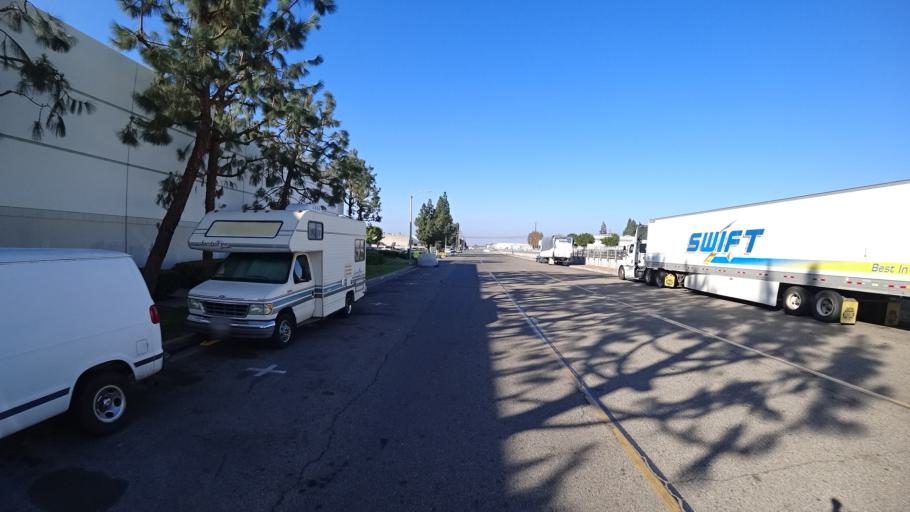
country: US
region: California
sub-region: Orange County
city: Placentia
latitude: 33.8668
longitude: -117.8958
